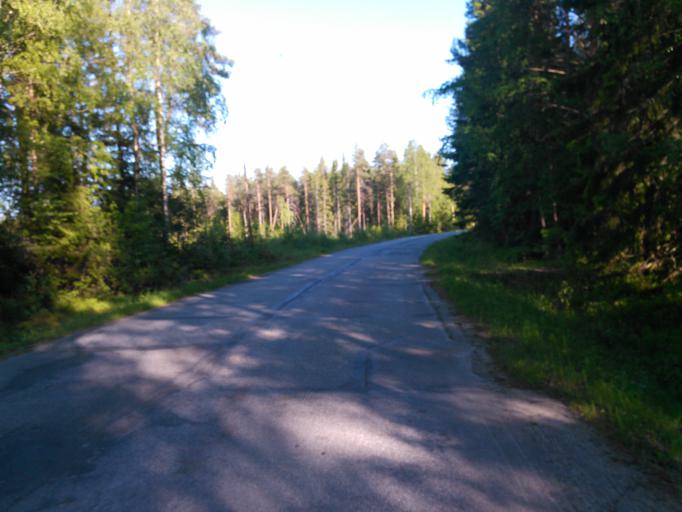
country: SE
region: Vaesterbotten
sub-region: Umea Kommun
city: Ersmark
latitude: 63.8764
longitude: 20.3238
